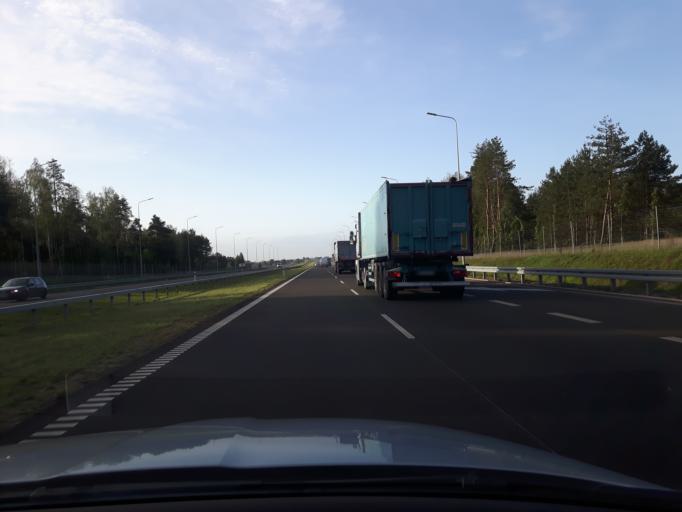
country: PL
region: Masovian Voivodeship
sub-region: Powiat radomski
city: Zakrzew
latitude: 51.4381
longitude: 21.0334
